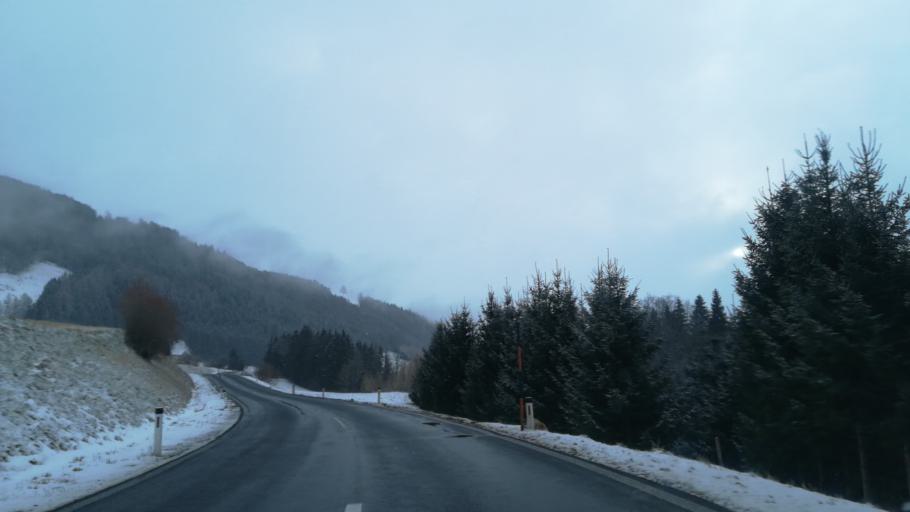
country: AT
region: Styria
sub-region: Politischer Bezirk Murtal
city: Poels
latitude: 47.2181
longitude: 14.6088
